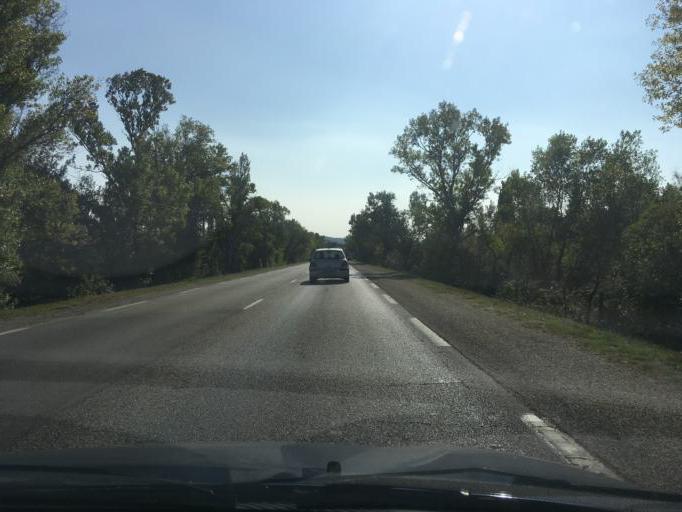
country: FR
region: Languedoc-Roussillon
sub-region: Departement du Gard
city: Pujaut
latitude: 44.0001
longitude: 4.7377
